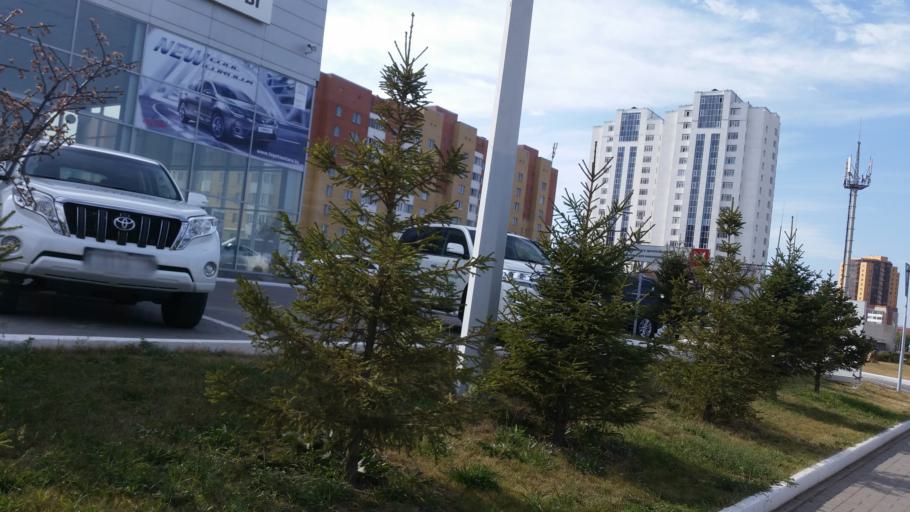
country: KZ
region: Astana Qalasy
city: Astana
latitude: 51.1633
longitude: 71.4807
